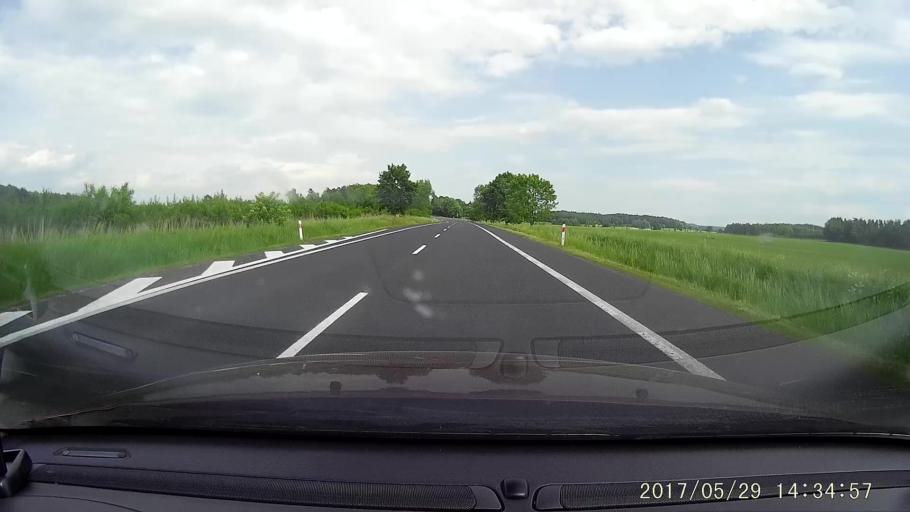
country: PL
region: Lower Silesian Voivodeship
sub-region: Powiat zgorzelecki
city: Piensk
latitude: 51.2040
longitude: 15.1290
